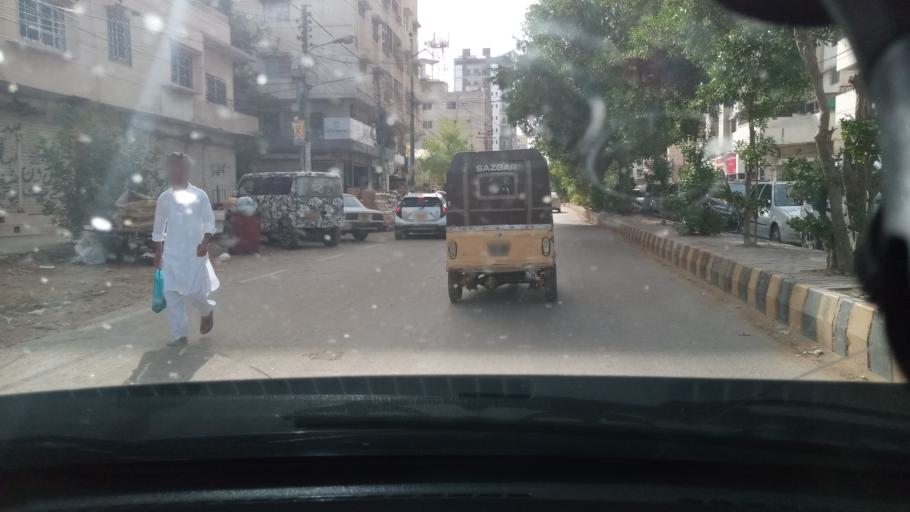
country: PK
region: Sindh
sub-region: Karachi District
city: Karachi
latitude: 24.8729
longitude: 67.0578
